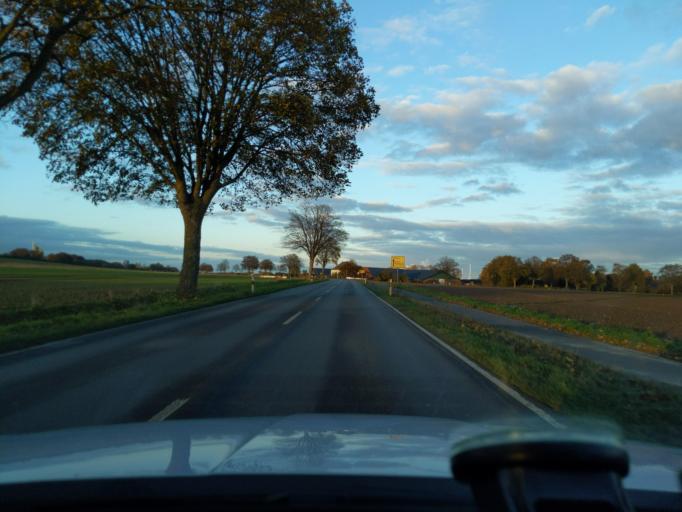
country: DE
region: North Rhine-Westphalia
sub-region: Regierungsbezirk Dusseldorf
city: Uedem
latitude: 51.6842
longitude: 6.3183
